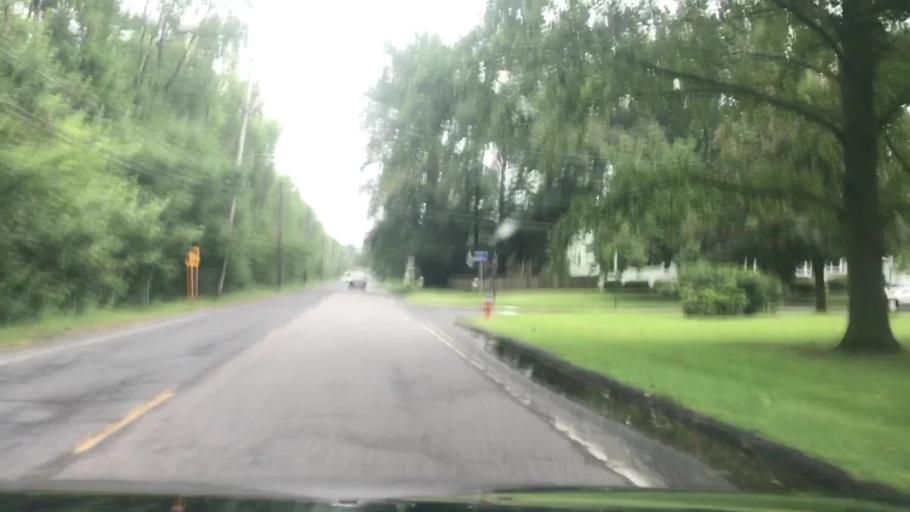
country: US
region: New Jersey
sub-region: Monmouth County
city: Oceanport
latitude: 40.3184
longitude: -74.0157
